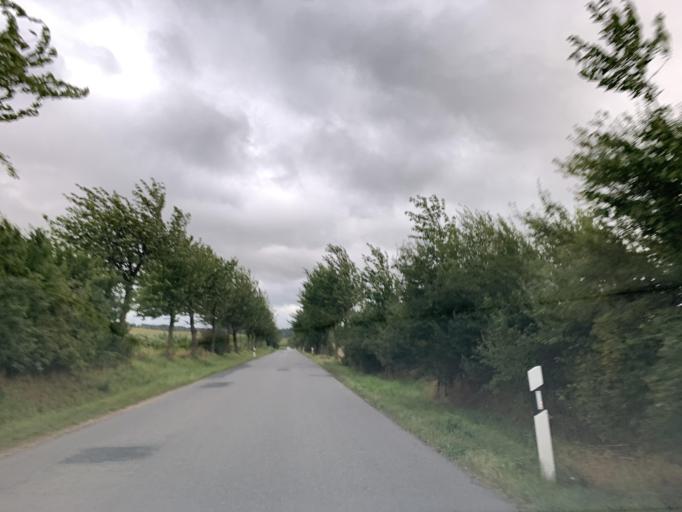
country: DE
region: Mecklenburg-Vorpommern
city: Loitz
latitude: 53.3457
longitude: 13.3913
